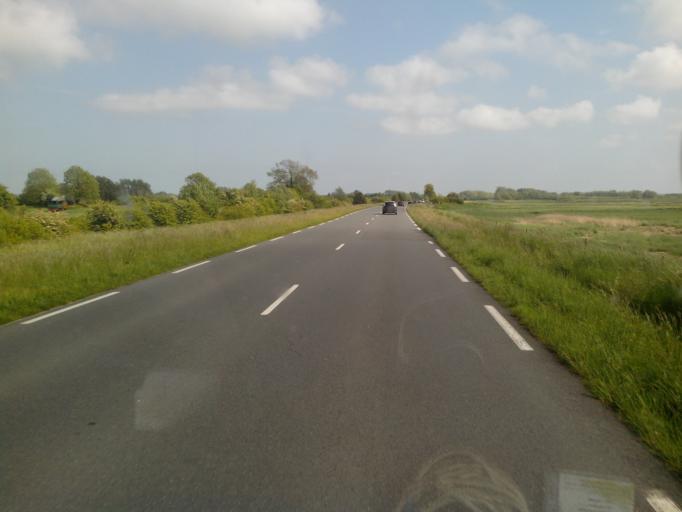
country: FR
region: Picardie
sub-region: Departement de la Somme
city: Saint-Valery-sur-Somme
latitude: 50.2063
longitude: 1.6816
